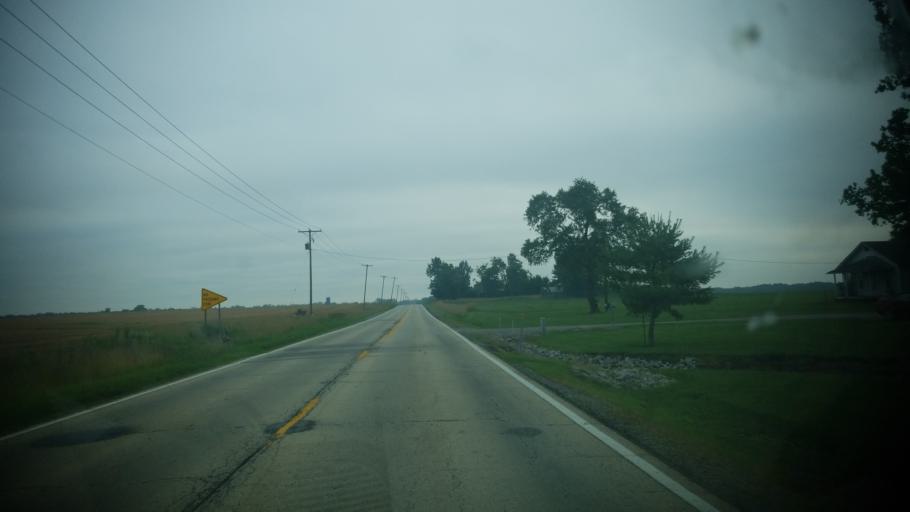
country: US
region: Illinois
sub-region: Clay County
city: Flora
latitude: 38.6556
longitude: -88.4384
